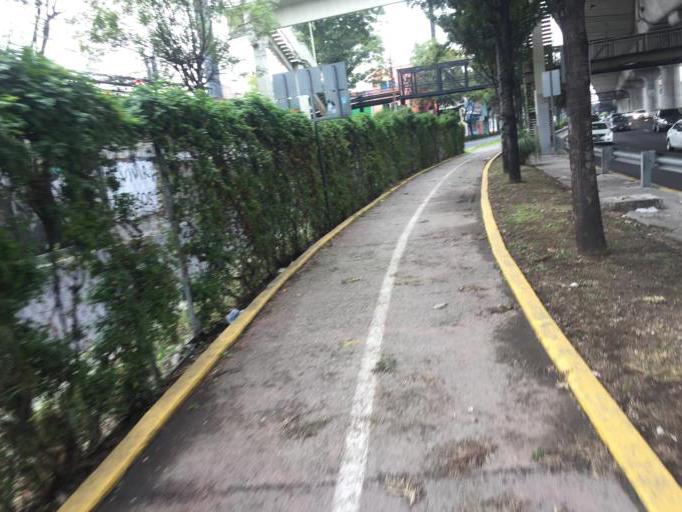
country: MX
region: Mexico City
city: Polanco
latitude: 19.4085
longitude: -99.1943
